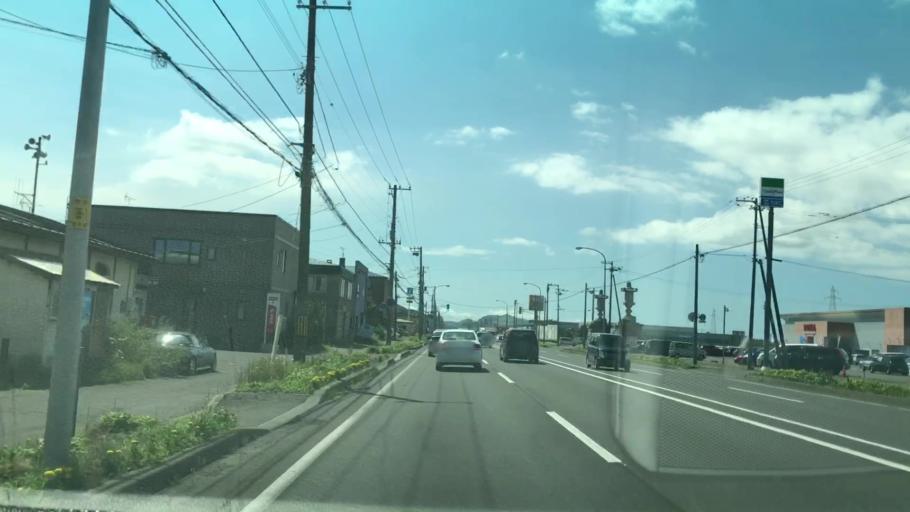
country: JP
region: Hokkaido
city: Muroran
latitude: 42.3725
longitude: 141.0654
